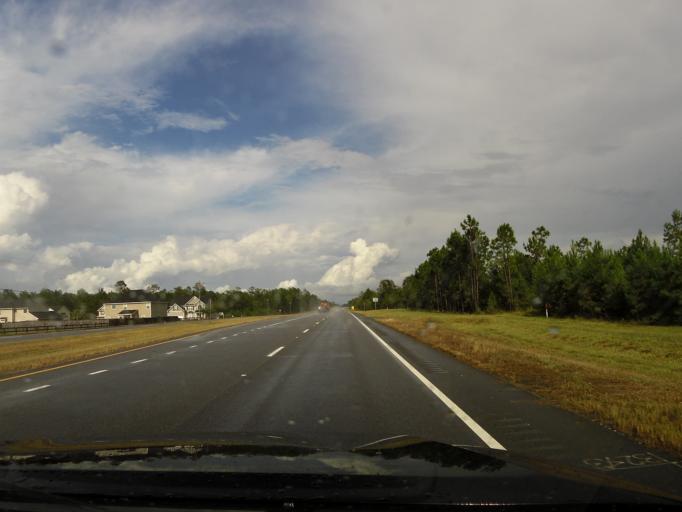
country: US
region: Georgia
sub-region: Liberty County
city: Walthourville
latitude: 31.7564
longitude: -81.6650
